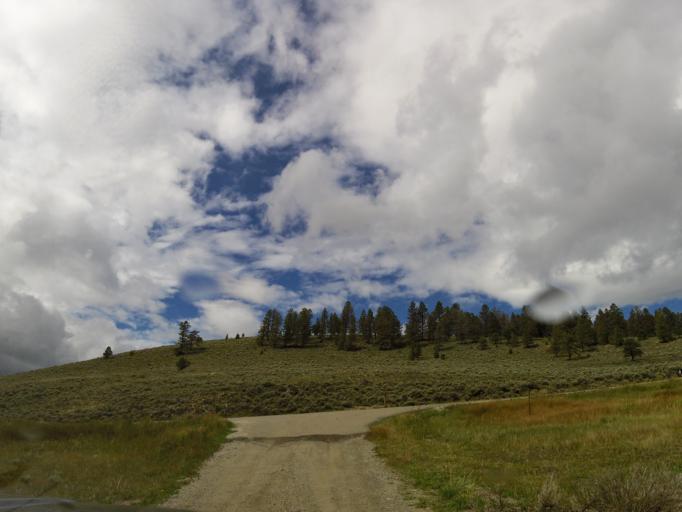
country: US
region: Colorado
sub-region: Chaffee County
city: Salida
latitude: 38.4050
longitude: -106.0672
